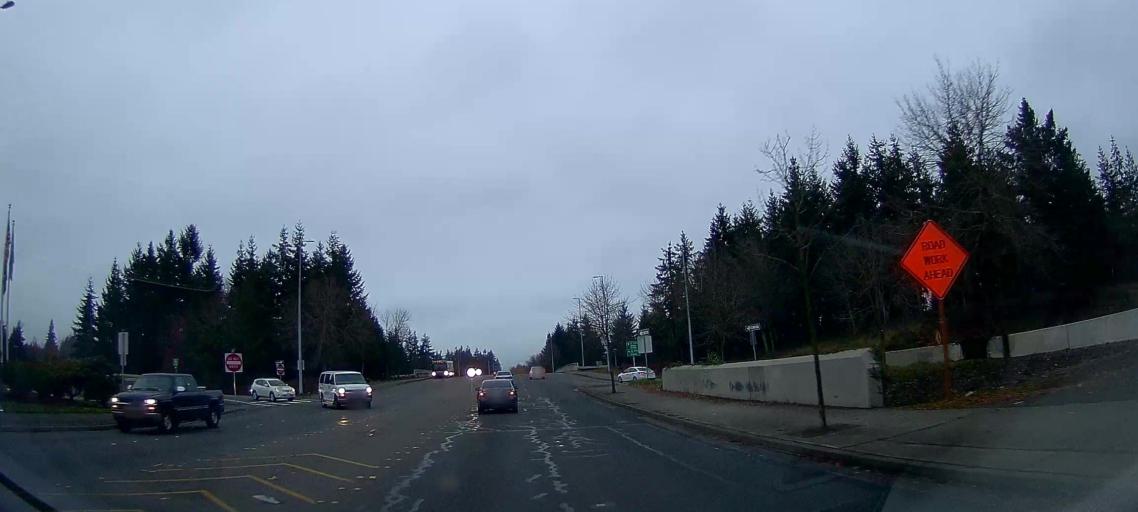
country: US
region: Washington
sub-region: Thurston County
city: Lacey
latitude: 47.0443
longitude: -122.8337
